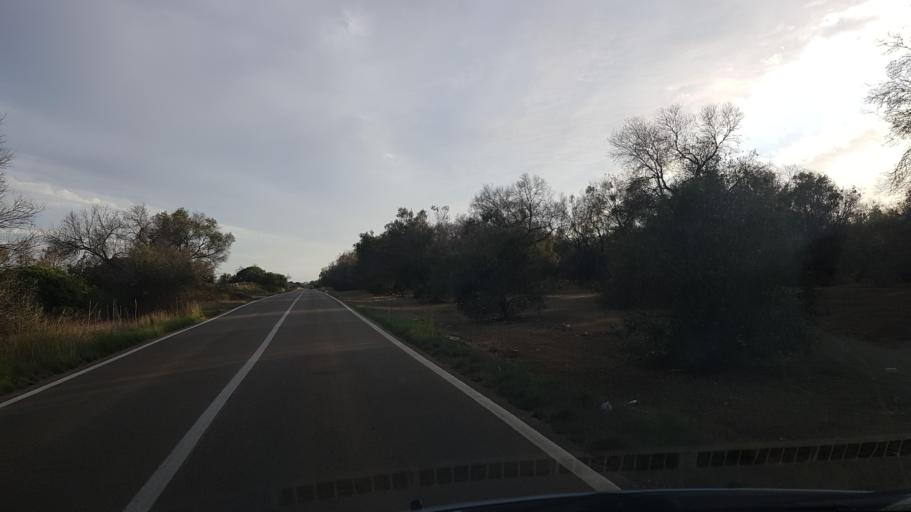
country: IT
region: Apulia
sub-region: Provincia di Brindisi
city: Torchiarolo
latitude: 40.4714
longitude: 18.1204
